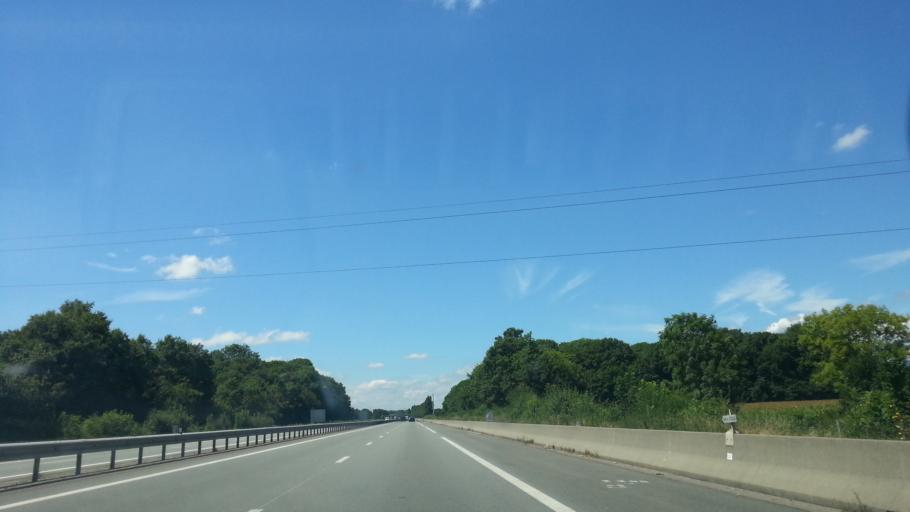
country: FR
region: Alsace
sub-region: Departement du Haut-Rhin
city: Reiningue
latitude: 47.7425
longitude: 7.2476
